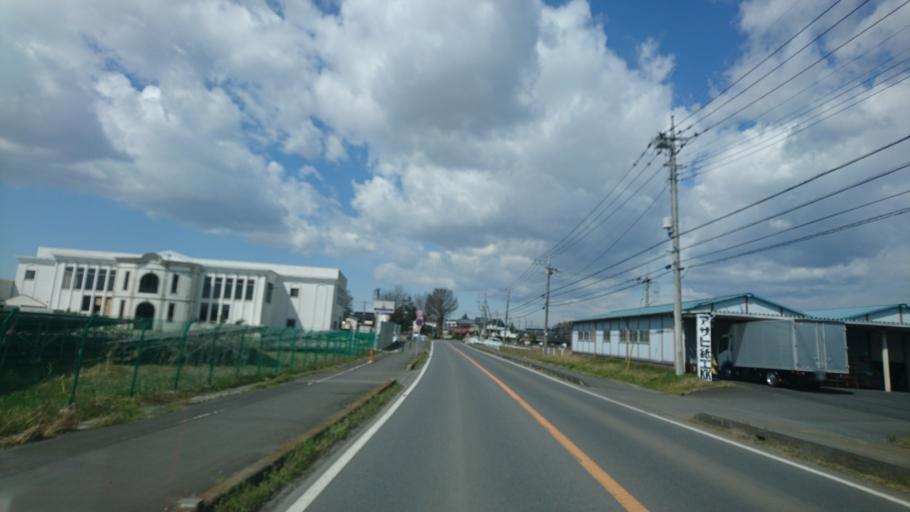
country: JP
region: Ibaraki
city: Ishige
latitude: 36.2018
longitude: 139.9481
